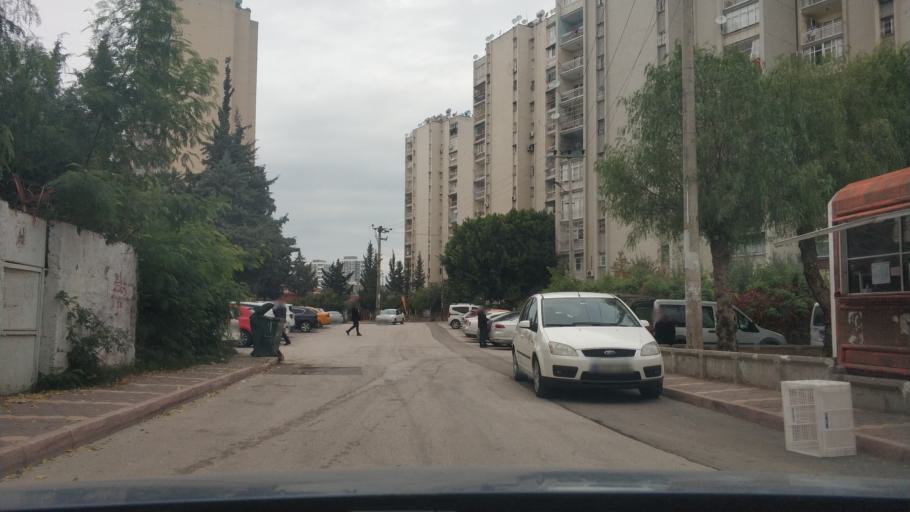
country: TR
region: Adana
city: Yuregir
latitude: 37.0042
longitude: 35.3614
